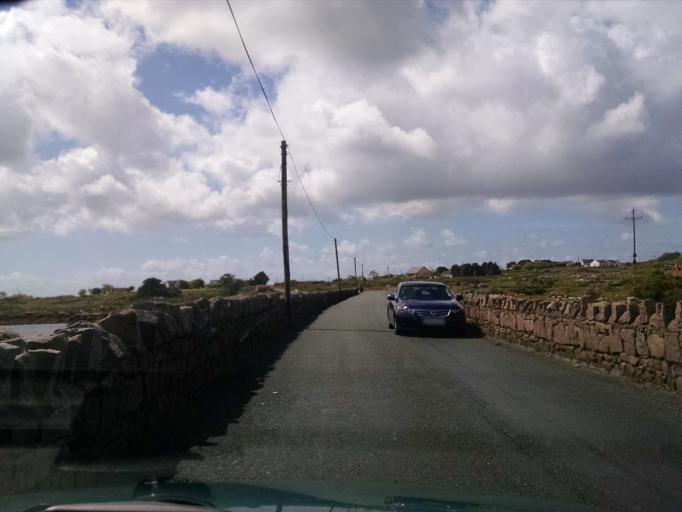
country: IE
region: Connaught
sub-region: County Galway
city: Oughterard
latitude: 53.3033
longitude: -9.6357
